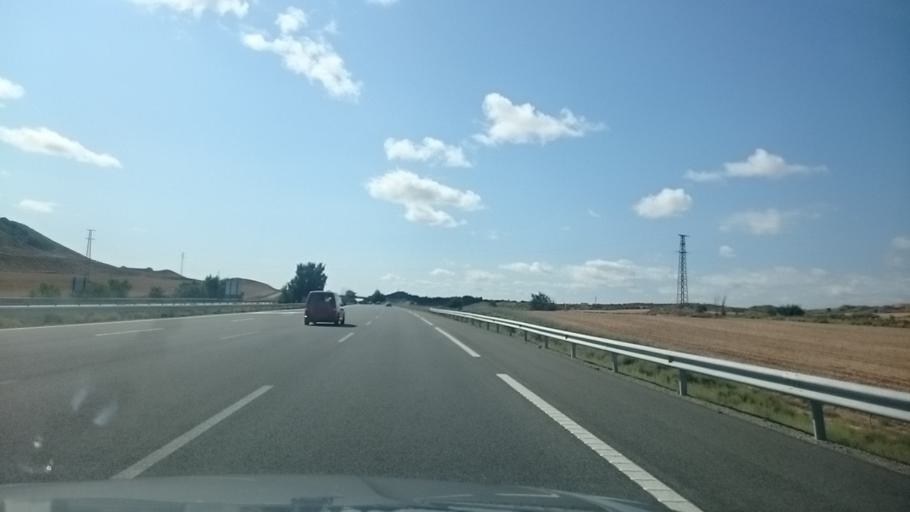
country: ES
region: Navarre
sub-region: Provincia de Navarra
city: Corella
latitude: 42.0904
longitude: -1.7186
